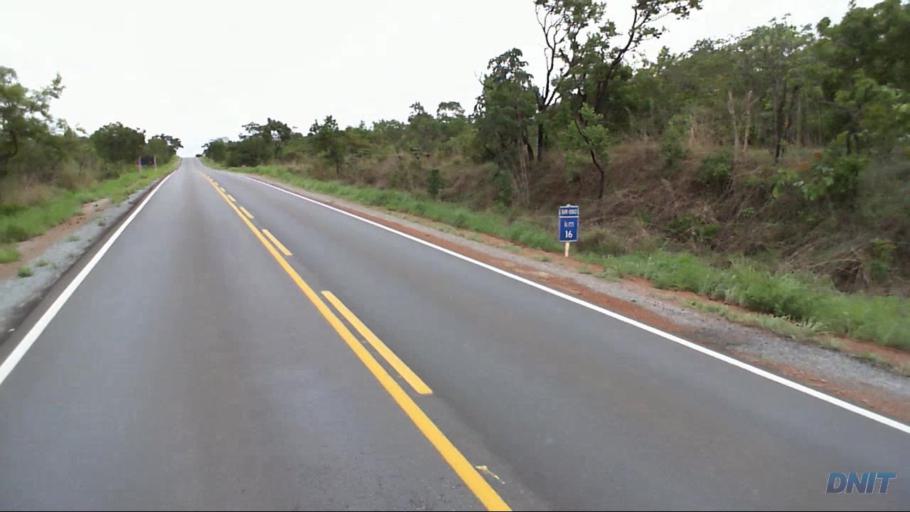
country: BR
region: Goias
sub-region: Padre Bernardo
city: Padre Bernardo
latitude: -15.4089
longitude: -48.2003
